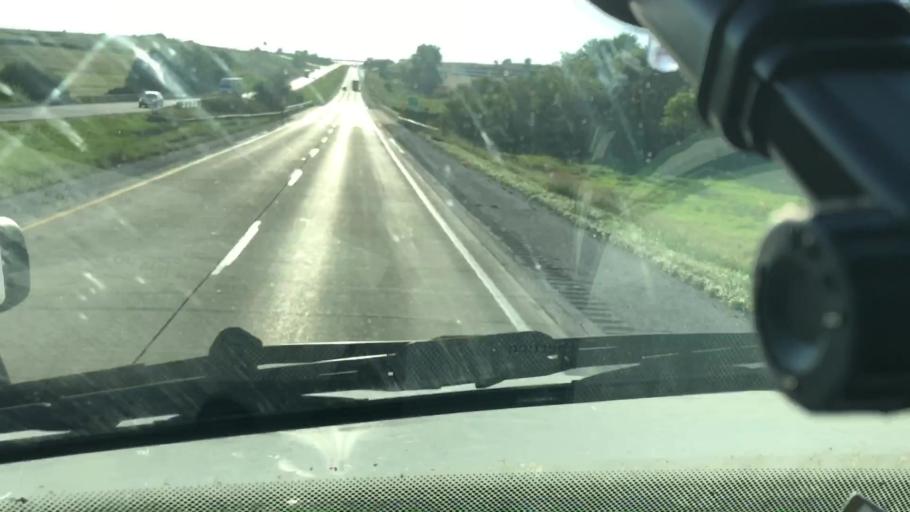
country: US
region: Iowa
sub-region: Pottawattamie County
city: Avoca
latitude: 41.5003
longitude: -95.5297
